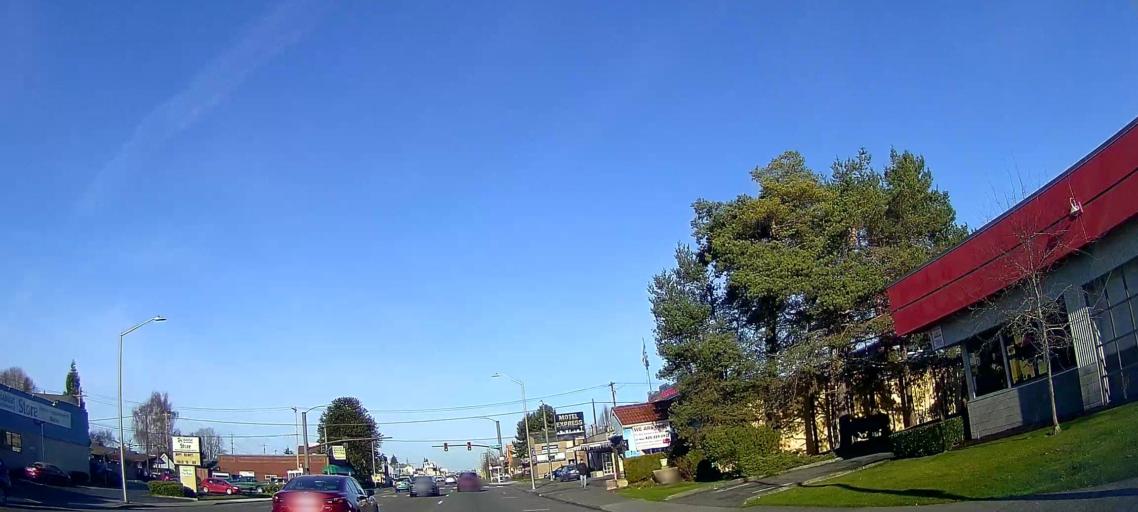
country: US
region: Washington
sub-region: Snohomish County
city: Everett
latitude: 47.9865
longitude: -122.2013
